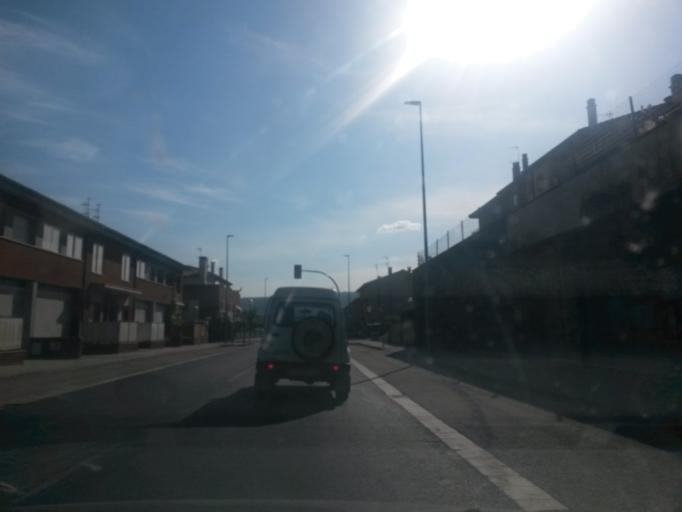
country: ES
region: Catalonia
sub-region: Provincia de Girona
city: Olot
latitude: 42.1675
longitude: 2.4766
